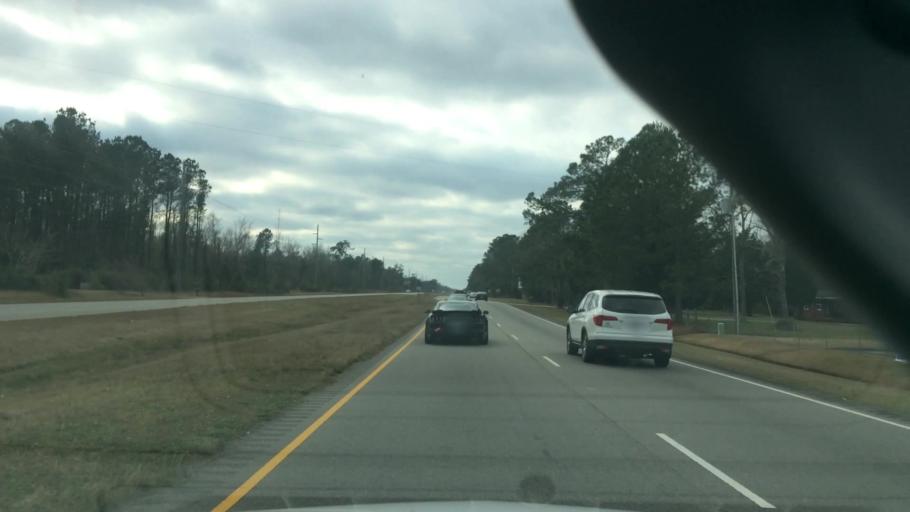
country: US
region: North Carolina
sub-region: Brunswick County
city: Shallotte
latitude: 34.0057
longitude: -78.3062
